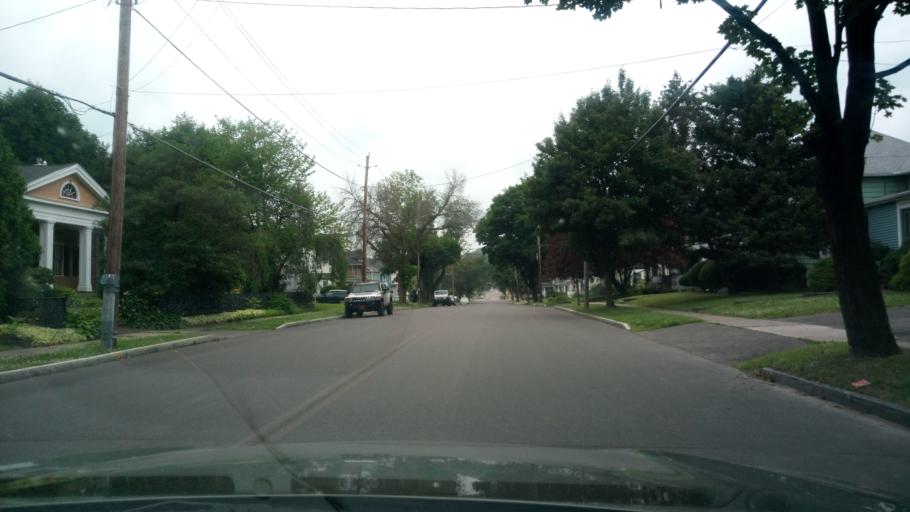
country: US
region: New York
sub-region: Chemung County
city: Elmira
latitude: 42.0983
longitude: -76.8164
